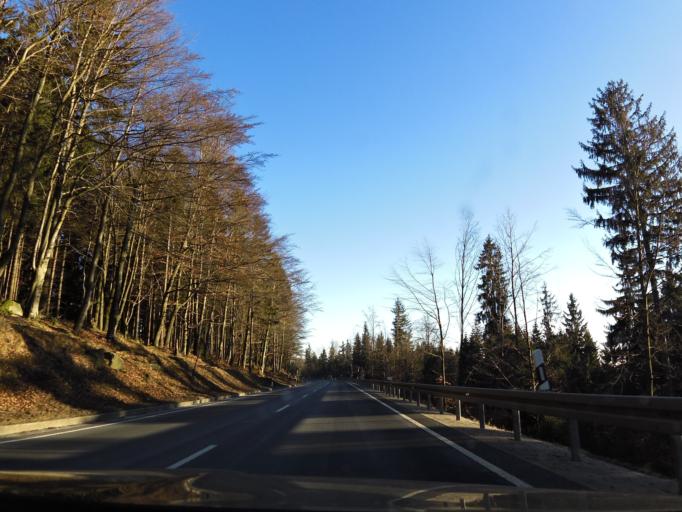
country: DE
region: Bavaria
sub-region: Upper Franconia
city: Fichtelberg
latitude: 50.0065
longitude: 11.8896
